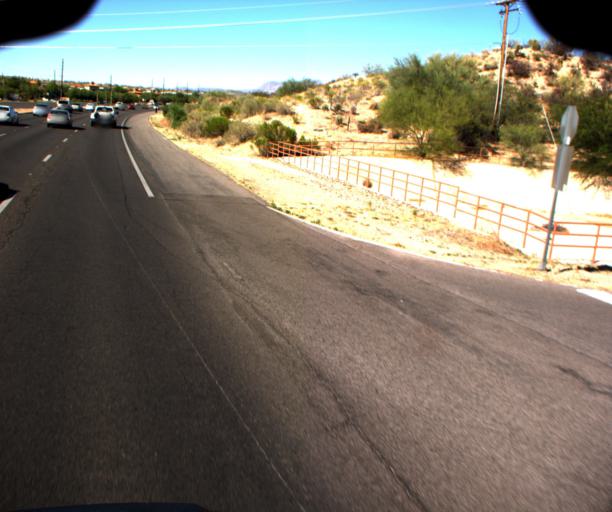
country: US
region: Arizona
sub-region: Pima County
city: Oro Valley
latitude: 32.3915
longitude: -110.9632
